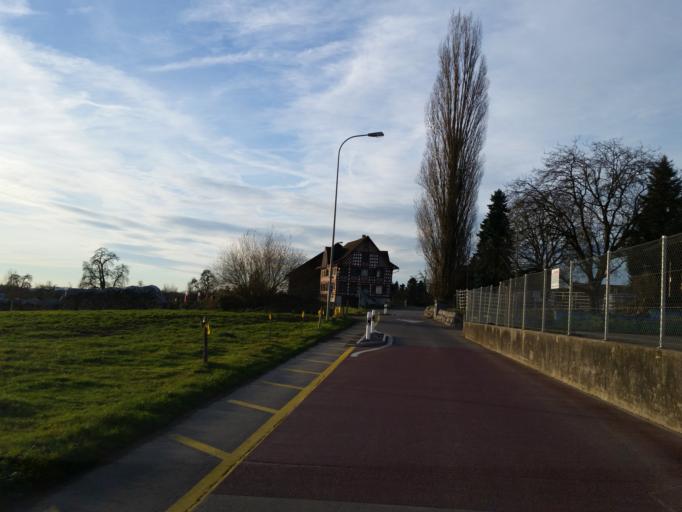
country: CH
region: Thurgau
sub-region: Arbon District
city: Amriswil
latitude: 47.5624
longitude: 9.3145
